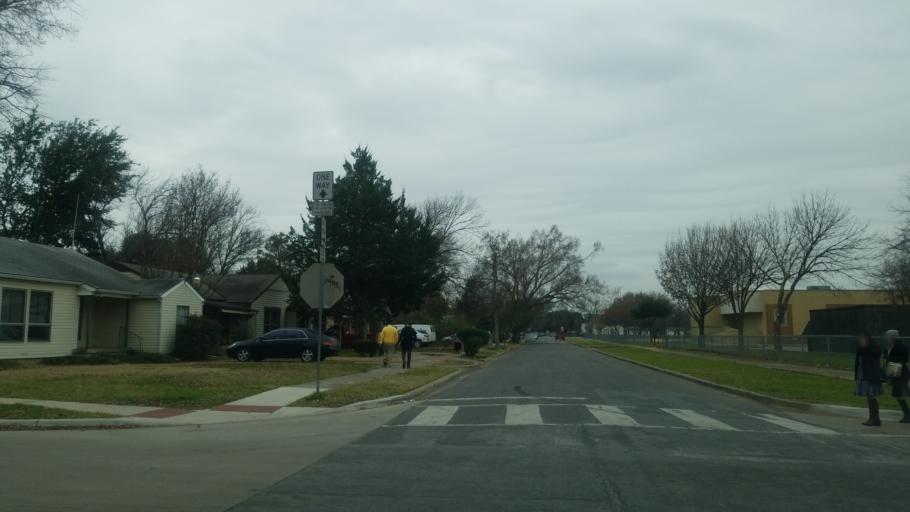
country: US
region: Texas
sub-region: Dallas County
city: University Park
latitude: 32.8260
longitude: -96.8279
